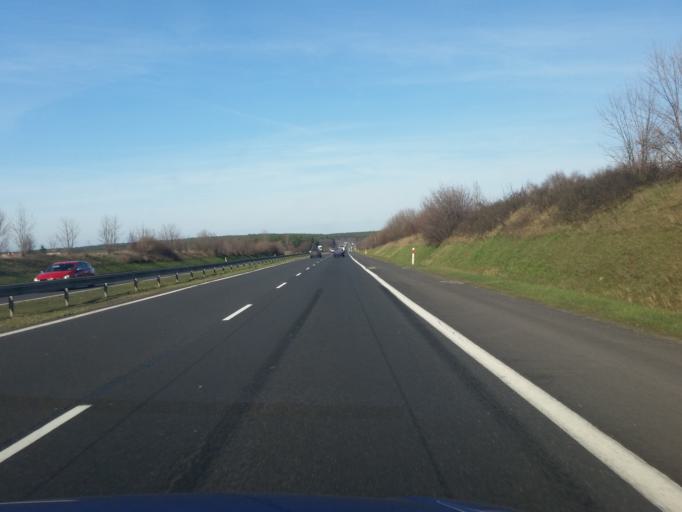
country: PL
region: Lodz Voivodeship
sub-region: Powiat radomszczanski
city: Gomunice
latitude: 51.1454
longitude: 19.4313
